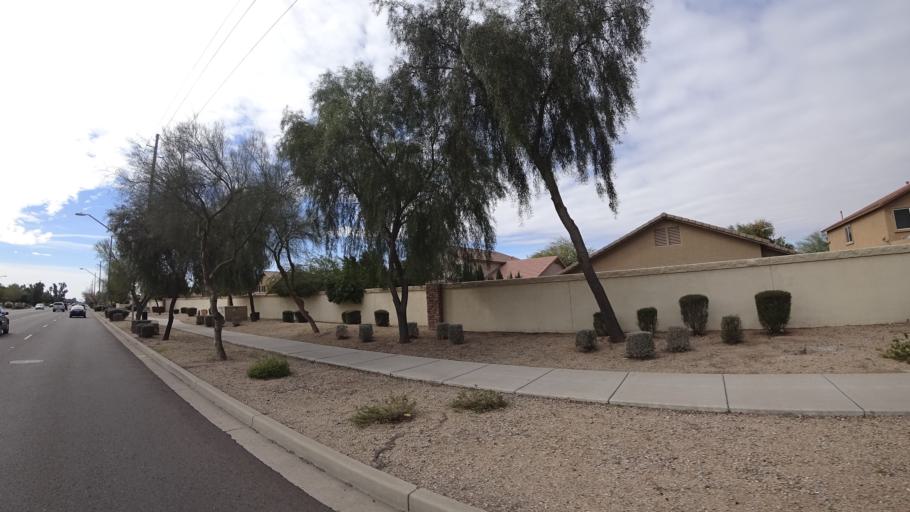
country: US
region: Arizona
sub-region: Maricopa County
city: Peoria
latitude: 33.6525
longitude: -112.1865
